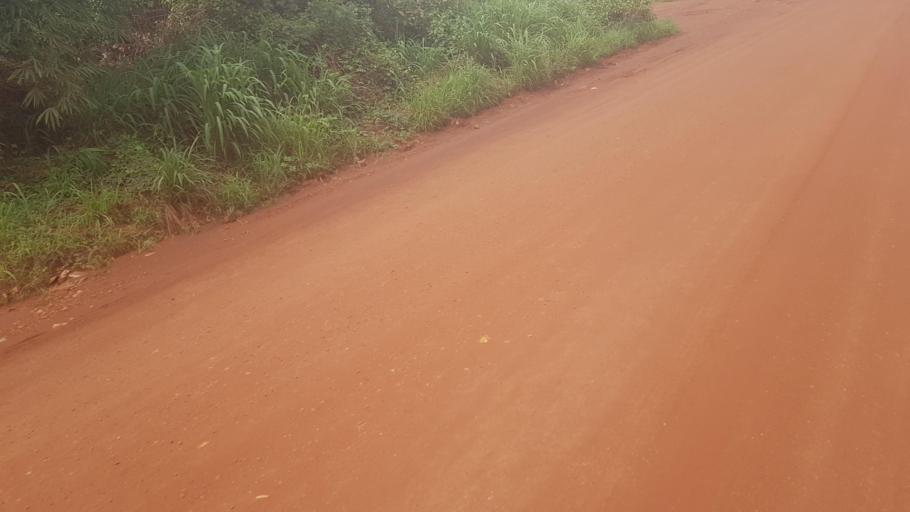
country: SL
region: Southern Province
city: Mogbwemo
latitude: 7.7636
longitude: -12.3044
